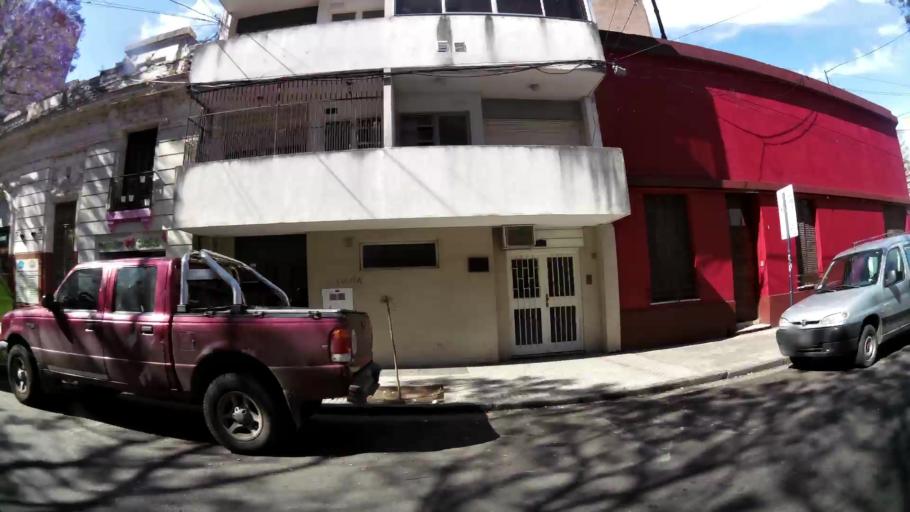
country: AR
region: Santa Fe
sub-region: Departamento de Rosario
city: Rosario
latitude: -32.9550
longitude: -60.6343
